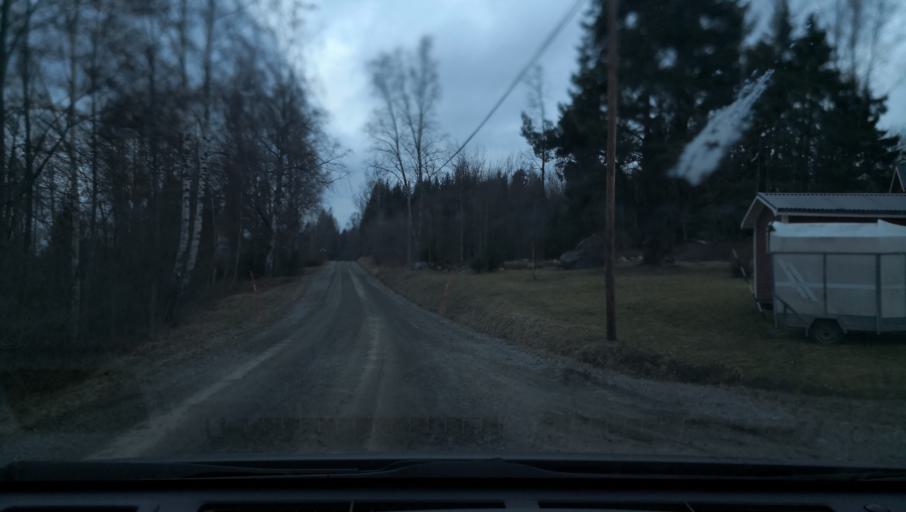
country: SE
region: Vaestmanland
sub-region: Kopings Kommun
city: Kolsva
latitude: 59.5924
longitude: 15.7196
